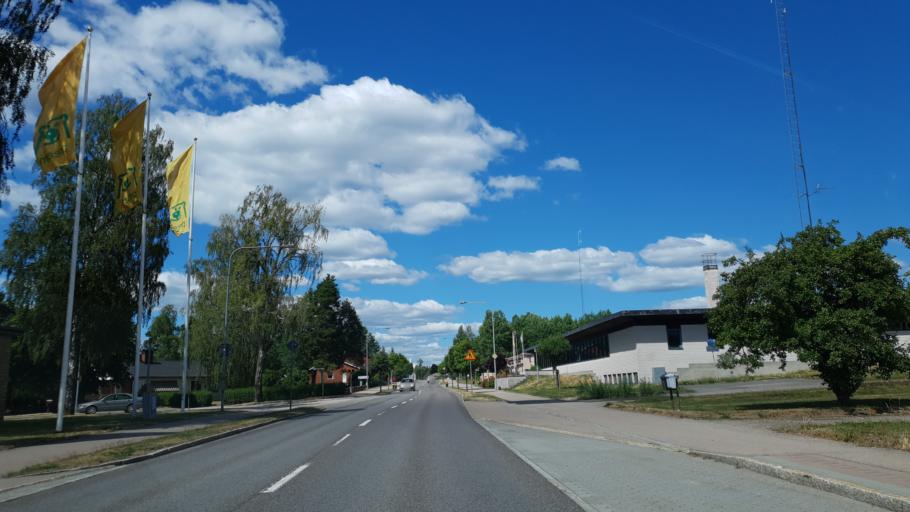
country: SE
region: Kronoberg
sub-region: Lessebo Kommun
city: Lessebo
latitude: 56.7563
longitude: 15.2672
